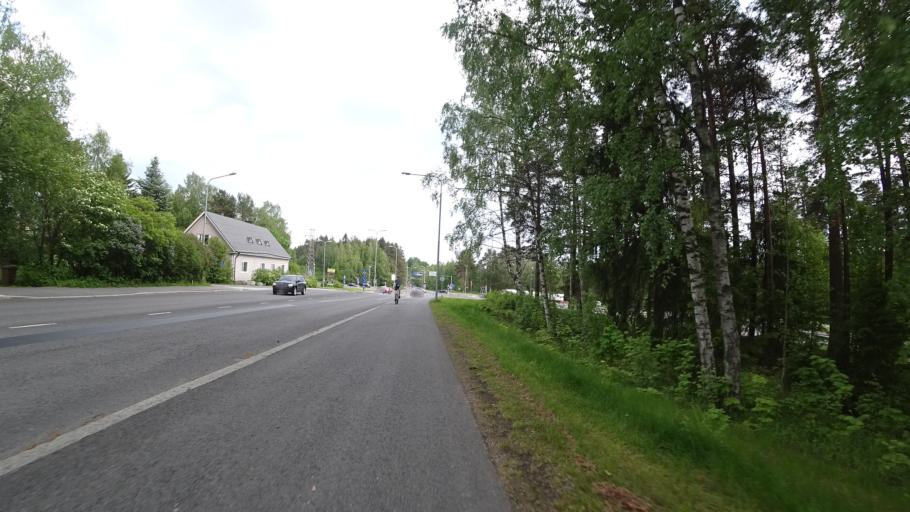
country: FI
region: Pirkanmaa
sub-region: Tampere
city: Yloejaervi
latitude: 61.5200
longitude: 23.6418
